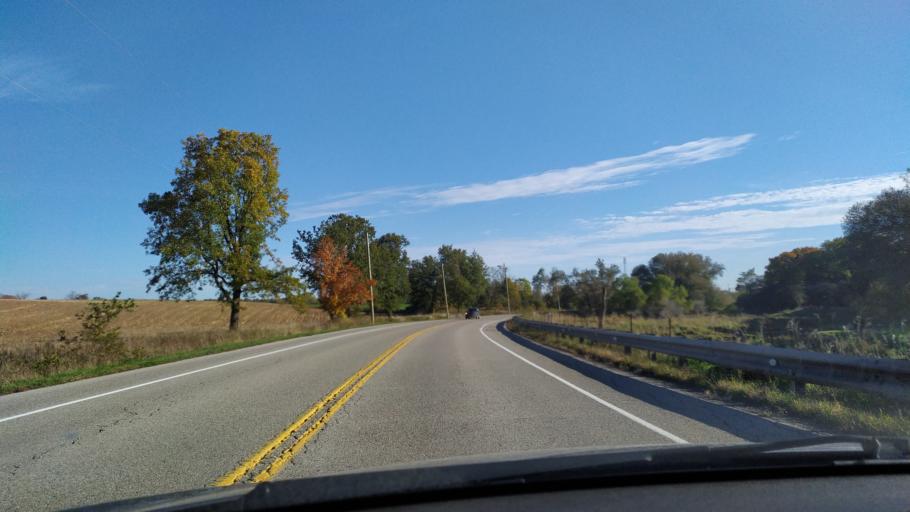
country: CA
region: Ontario
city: Stratford
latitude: 43.4699
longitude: -80.7918
